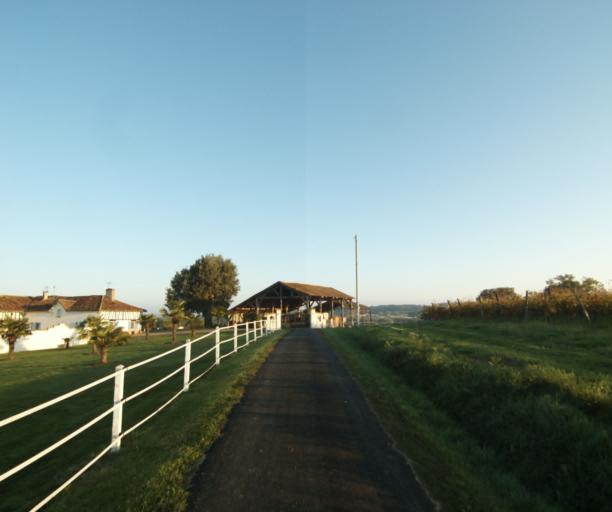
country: FR
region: Midi-Pyrenees
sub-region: Departement du Gers
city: Gondrin
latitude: 43.7843
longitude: 0.1869
